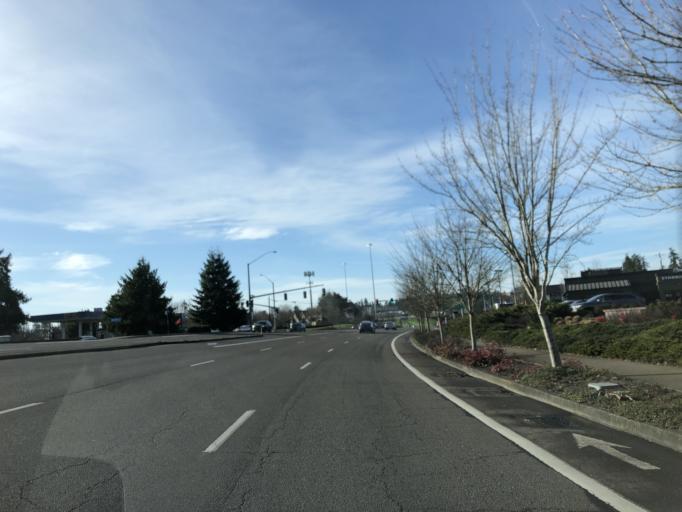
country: US
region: Oregon
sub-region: Washington County
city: Durham
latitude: 45.3970
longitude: -122.7423
